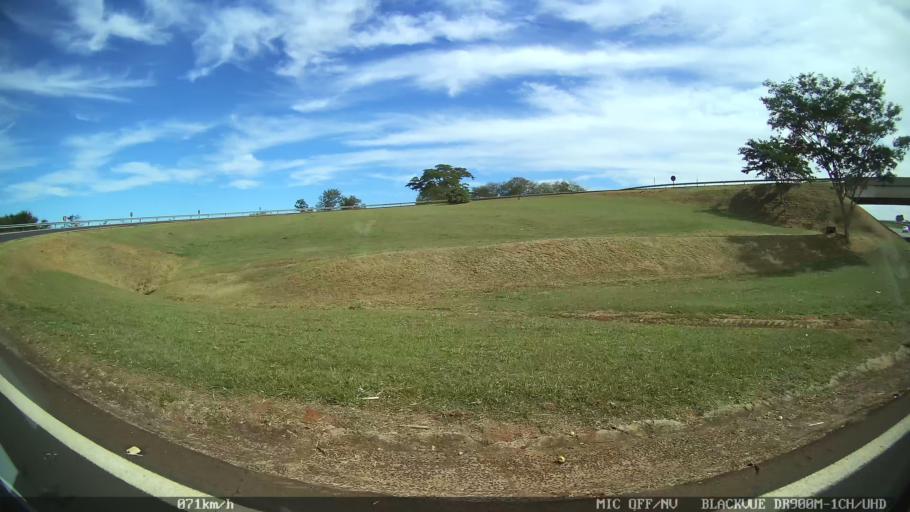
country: BR
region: Sao Paulo
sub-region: Taquaritinga
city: Taquaritinga
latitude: -21.5166
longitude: -48.5407
